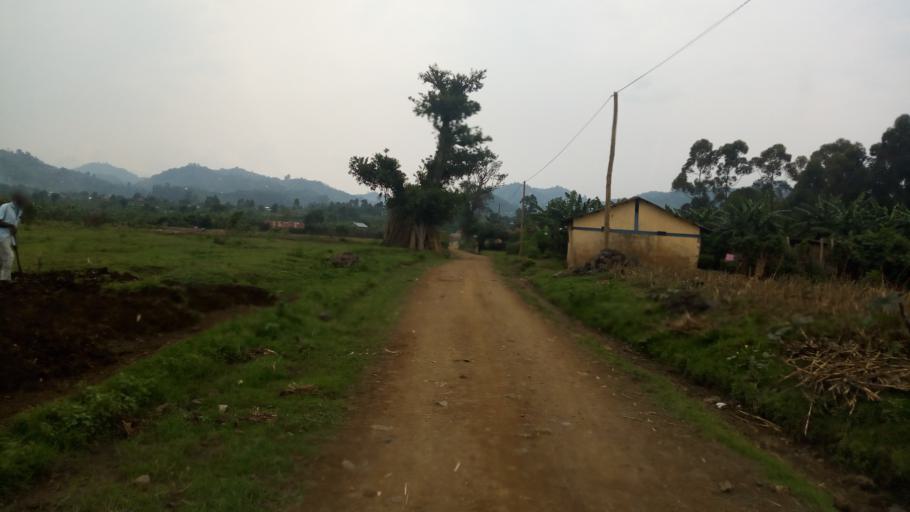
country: UG
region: Western Region
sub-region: Kisoro District
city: Kisoro
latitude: -1.2714
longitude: 29.6253
